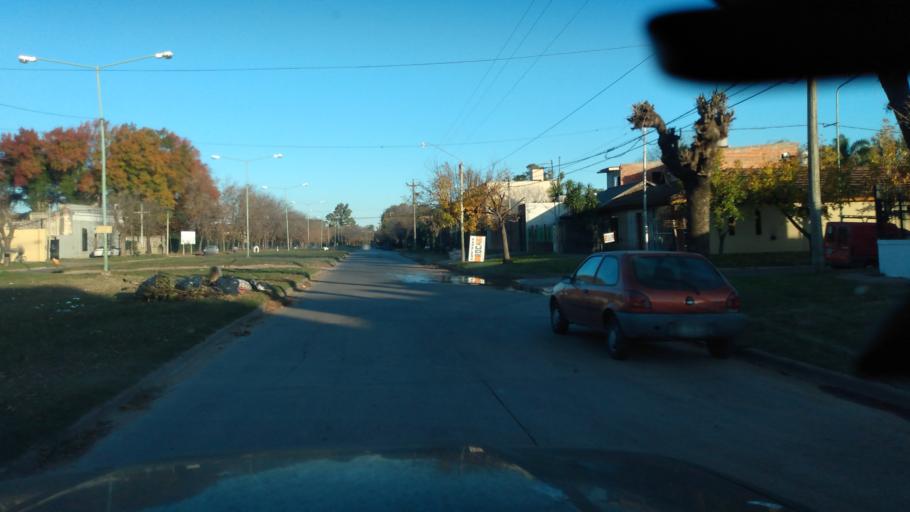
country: AR
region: Buenos Aires
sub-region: Partido de Lujan
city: Lujan
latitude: -34.5594
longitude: -59.1288
